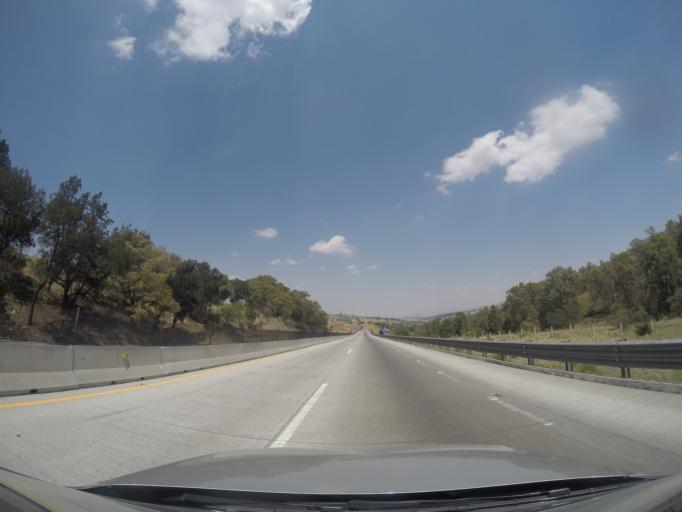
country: MX
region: Tlaxcala
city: Sanctorum
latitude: 19.4816
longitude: -98.4578
